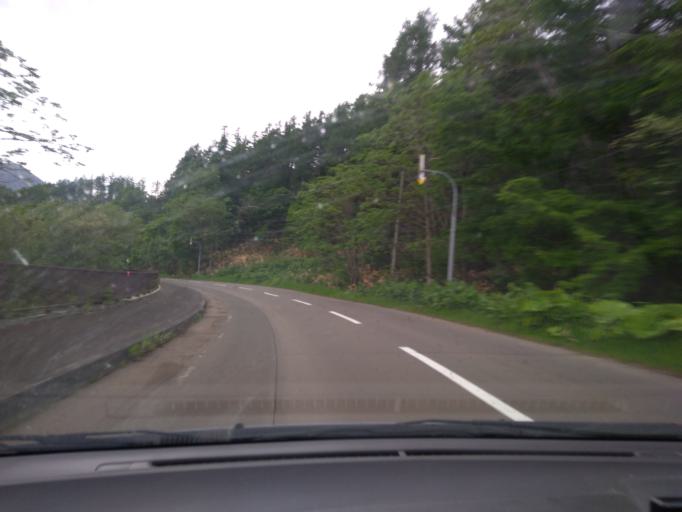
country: JP
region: Hokkaido
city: Shimo-furano
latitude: 43.1682
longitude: 142.5119
